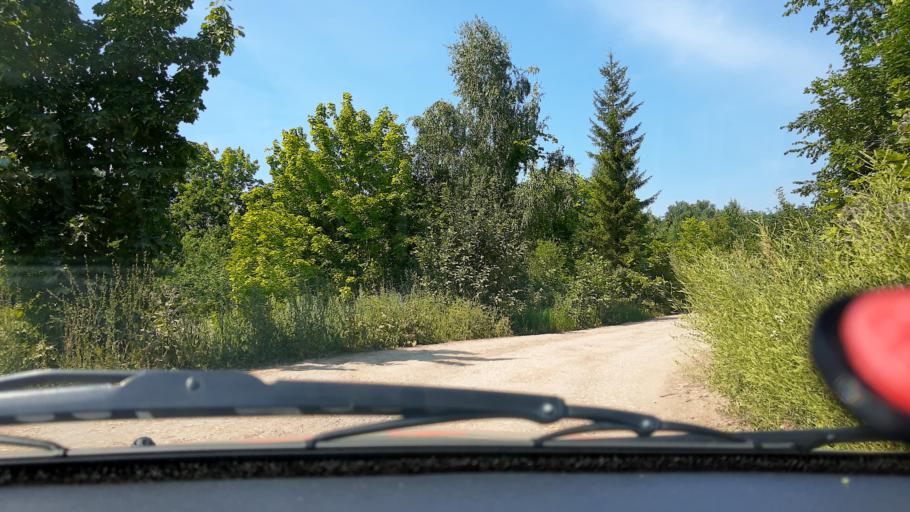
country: RU
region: Bashkortostan
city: Karmaskaly
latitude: 54.3883
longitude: 55.9016
